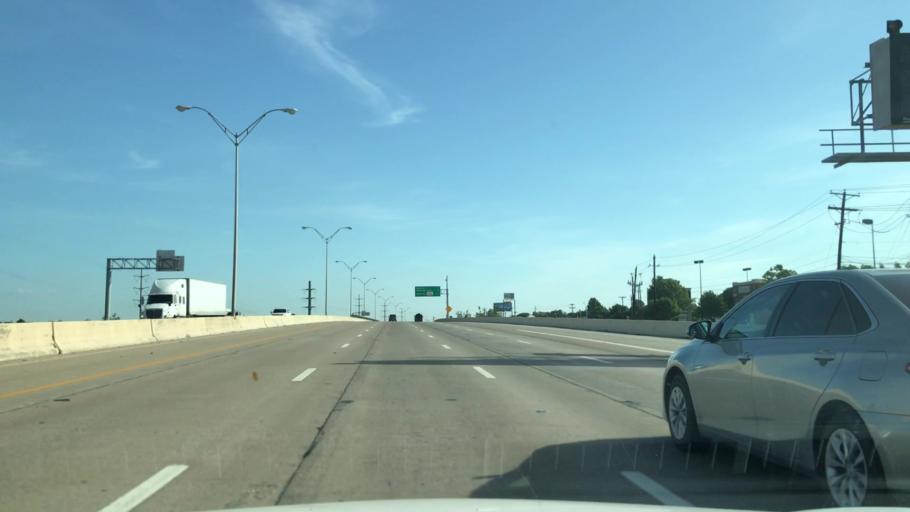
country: US
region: Texas
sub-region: Collin County
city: Allen
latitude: 33.0993
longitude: -96.6786
